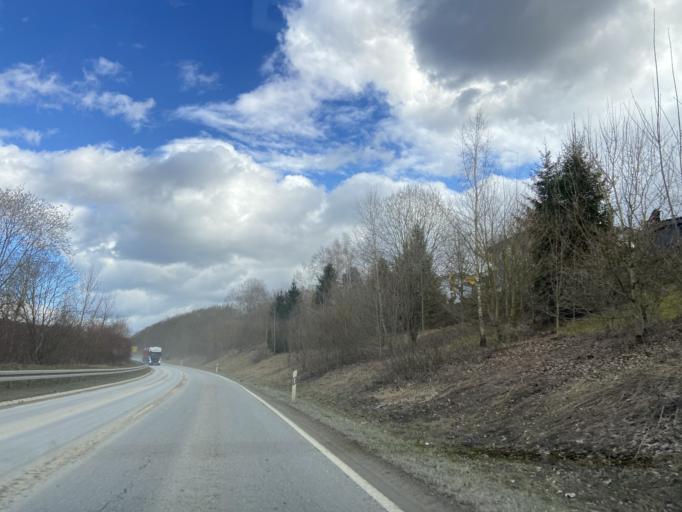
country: DE
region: Baden-Wuerttemberg
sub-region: Tuebingen Region
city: Ostrach
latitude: 47.9586
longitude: 9.3810
